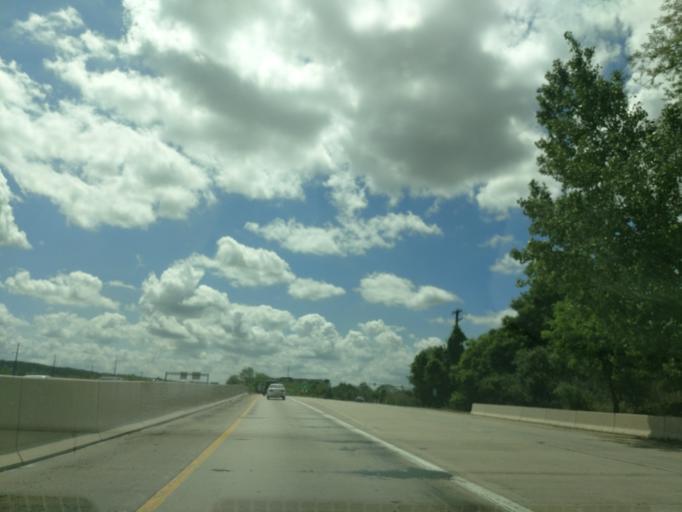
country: US
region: Pennsylvania
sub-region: Montgomery County
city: King of Prussia
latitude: 40.0812
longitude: -75.4041
